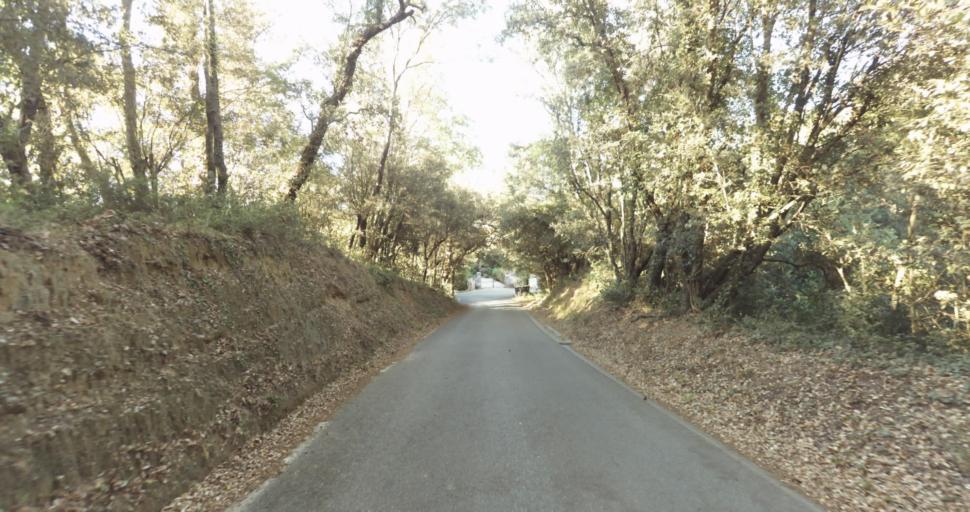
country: FR
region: Provence-Alpes-Cote d'Azur
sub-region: Departement du Var
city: Gassin
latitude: 43.2299
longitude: 6.5940
